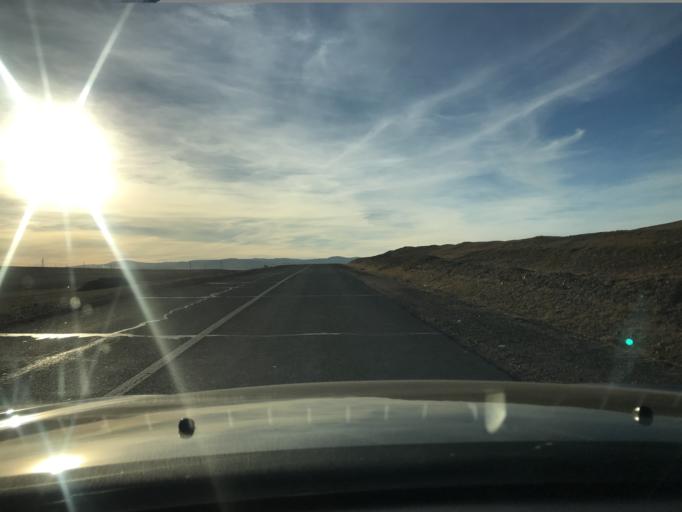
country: MN
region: Central Aimak
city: Dzuunmod
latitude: 47.7884
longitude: 107.3144
